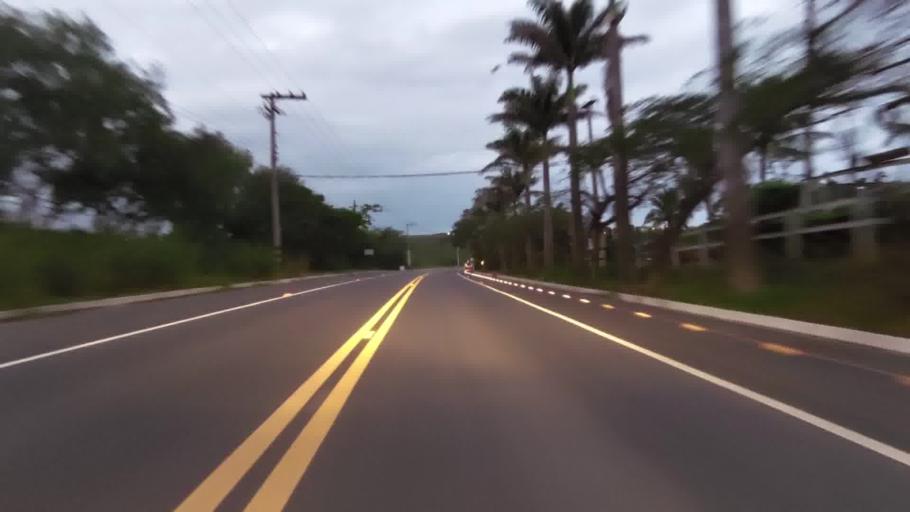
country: BR
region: Espirito Santo
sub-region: Piuma
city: Piuma
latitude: -20.8046
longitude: -40.6079
